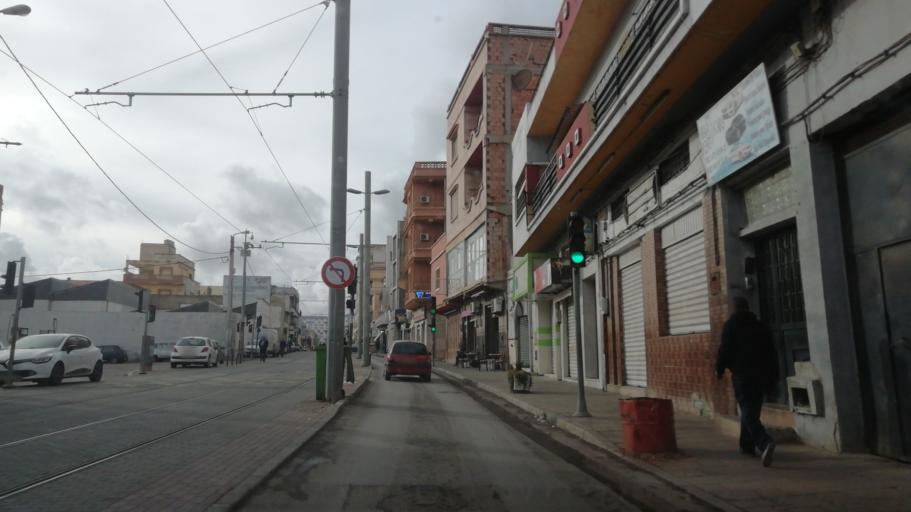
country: DZ
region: Oran
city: Oran
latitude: 35.6986
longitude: -0.6206
